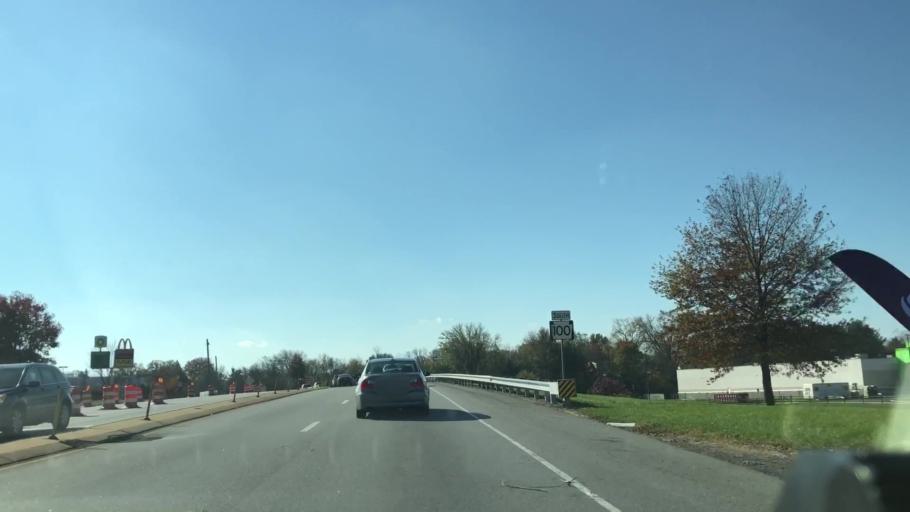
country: US
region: Pennsylvania
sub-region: Montgomery County
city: Pottstown
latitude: 40.2537
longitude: -75.6597
